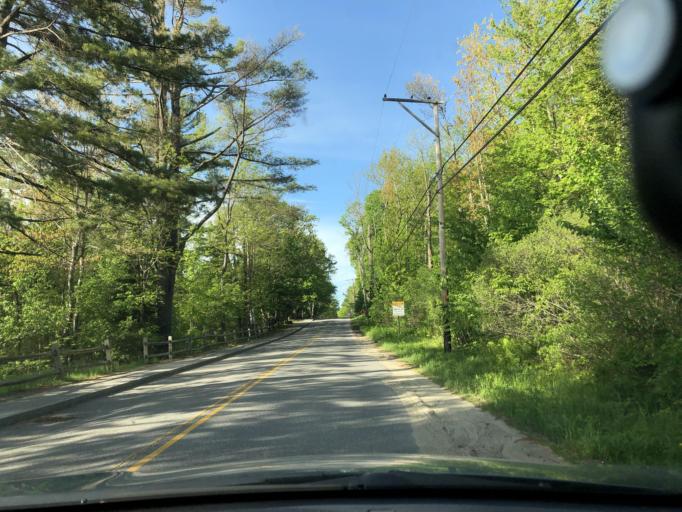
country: US
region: New Hampshire
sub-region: Merrimack County
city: New London
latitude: 43.4176
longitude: -71.9820
